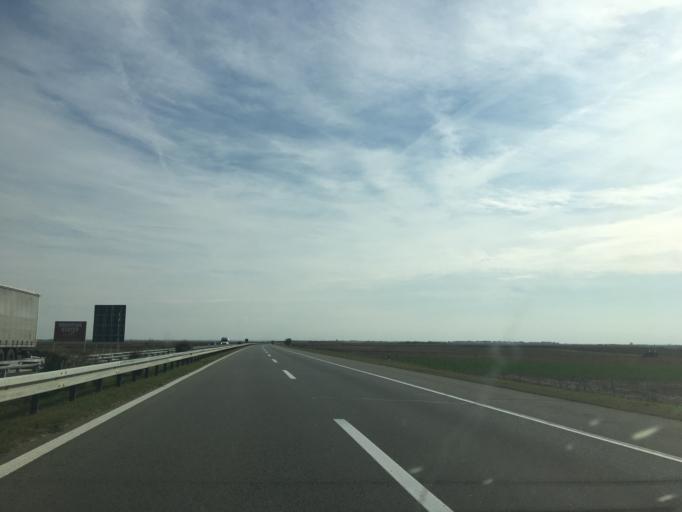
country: RS
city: Novi Karlovci
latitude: 45.0620
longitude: 20.1615
